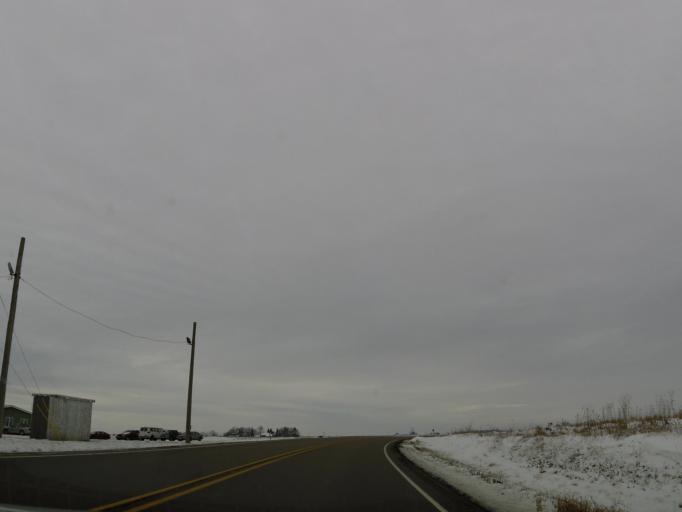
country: US
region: Illinois
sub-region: LaSalle County
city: Peru
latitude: 41.2578
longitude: -89.1346
